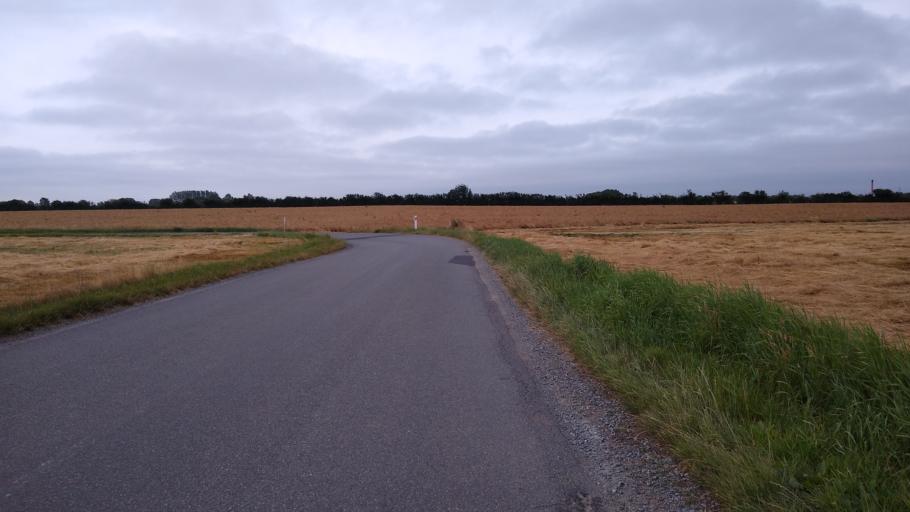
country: DK
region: South Denmark
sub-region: Vejle Kommune
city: Brejning
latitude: 55.6458
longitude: 9.6872
